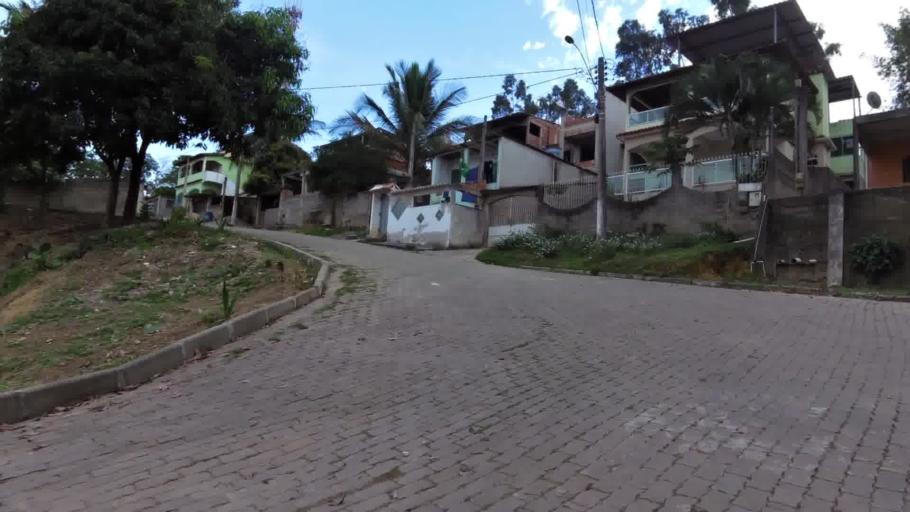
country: BR
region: Espirito Santo
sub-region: Piuma
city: Piuma
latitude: -20.8331
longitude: -40.7246
